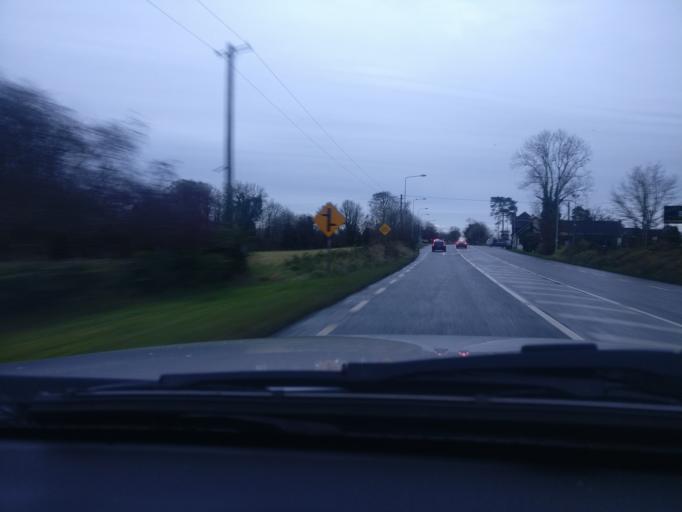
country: IE
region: Leinster
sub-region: An Mhi
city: Navan
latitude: 53.6873
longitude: -6.7702
